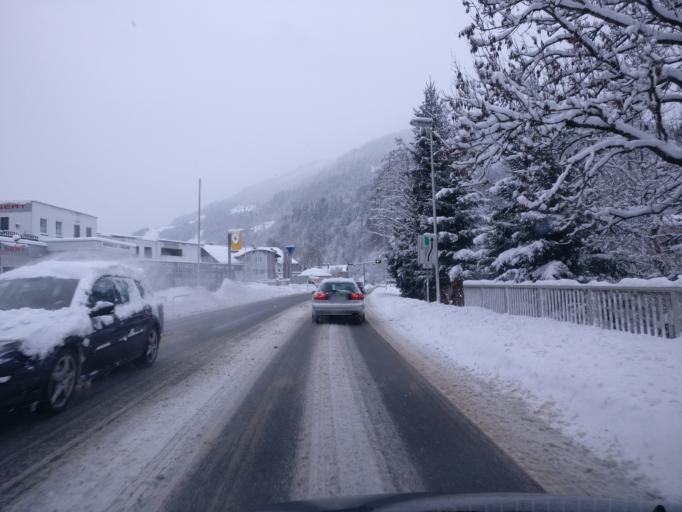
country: AT
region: Salzburg
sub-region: Politischer Bezirk Sankt Johann im Pongau
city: Bischofshofen
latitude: 47.3964
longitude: 13.2226
